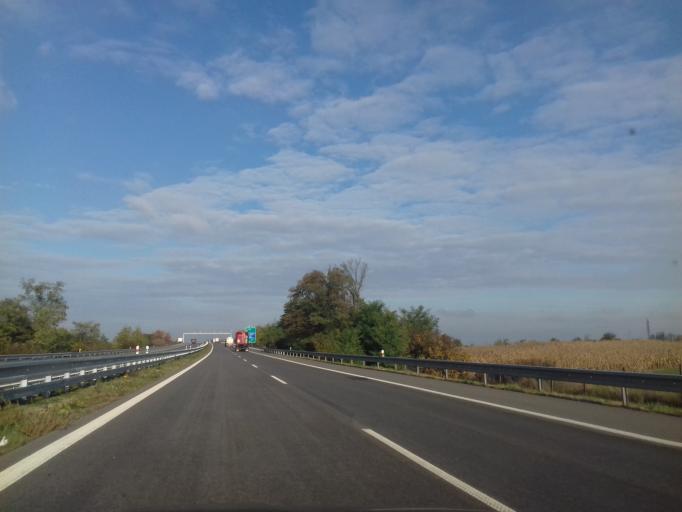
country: CZ
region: South Moravian
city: Hrusky
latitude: 48.7759
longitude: 16.9328
